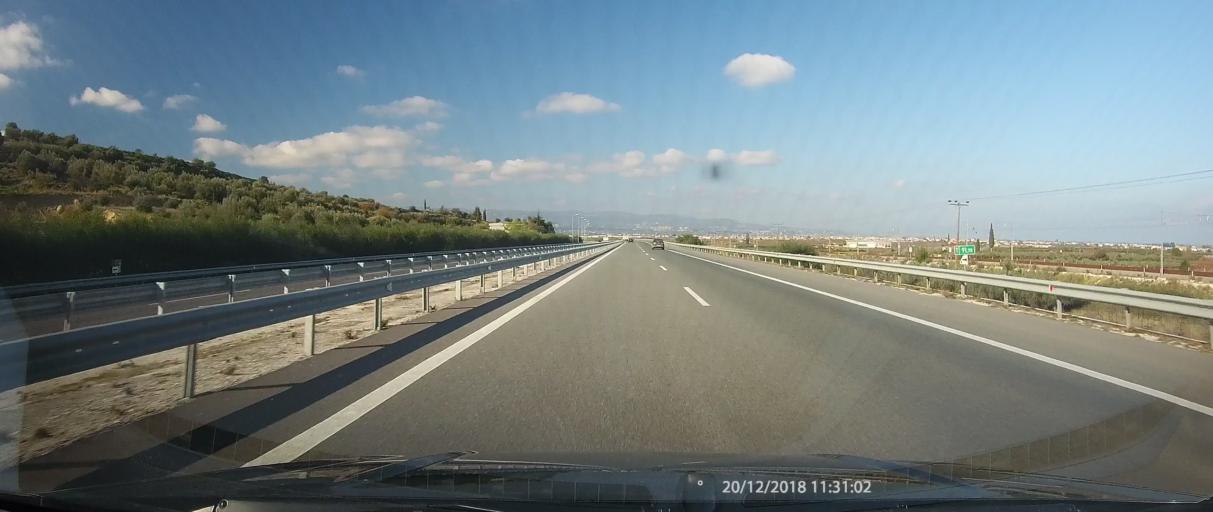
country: GR
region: Peloponnese
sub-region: Nomos Korinthias
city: Assos
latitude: 37.9184
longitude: 22.8233
